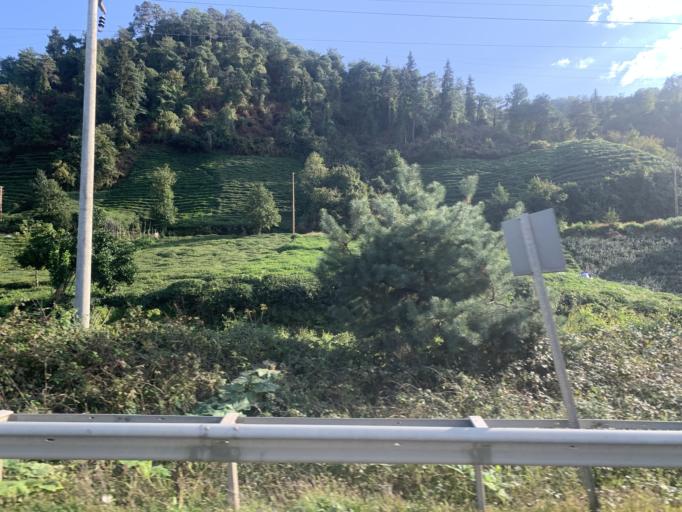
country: TR
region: Trabzon
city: Of
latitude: 40.9363
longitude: 40.2493
